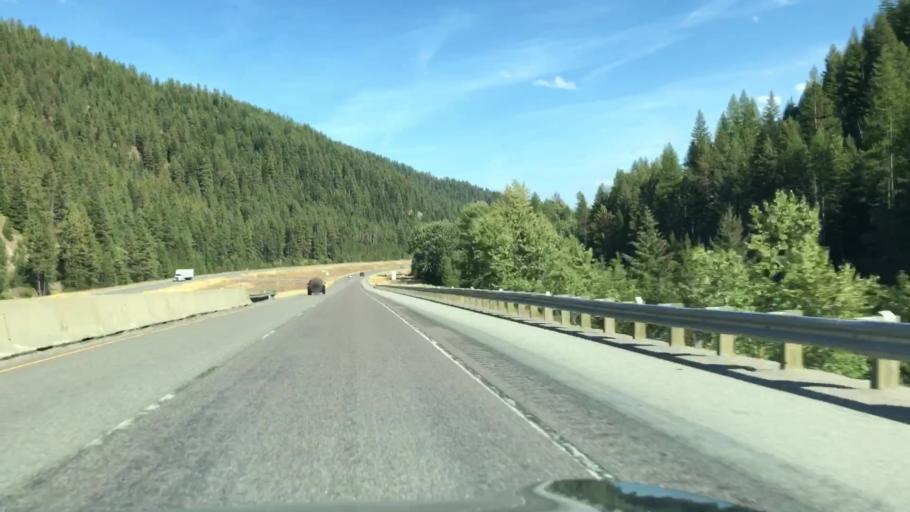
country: US
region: Montana
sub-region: Sanders County
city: Thompson Falls
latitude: 47.4075
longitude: -115.5008
